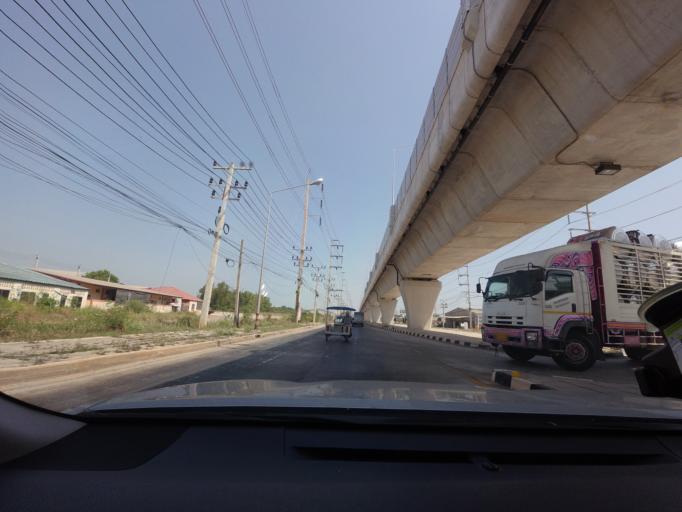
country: TH
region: Surat Thani
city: Surat Thani
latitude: 9.1523
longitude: 99.3690
